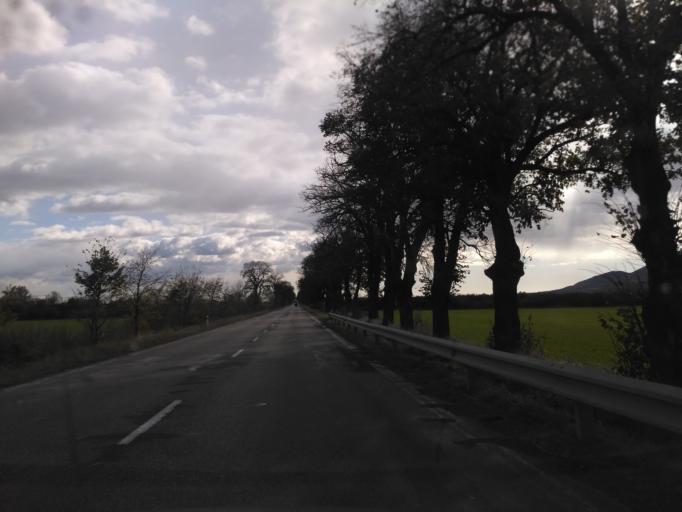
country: HU
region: Borsod-Abauj-Zemplen
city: Satoraljaujhely
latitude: 48.4564
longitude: 21.6457
